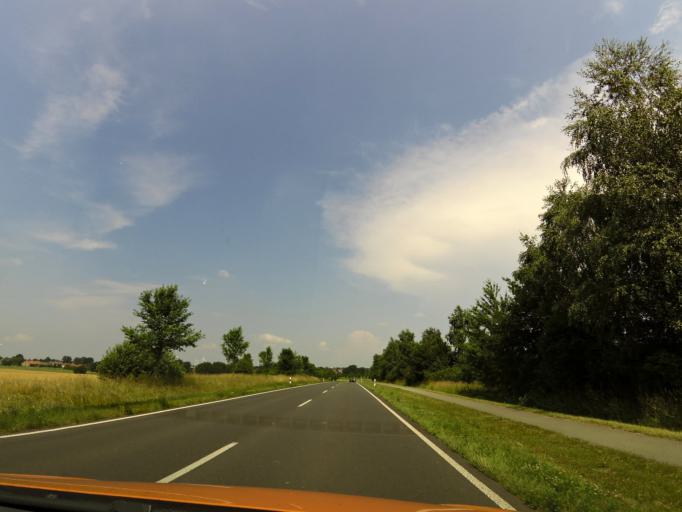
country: DE
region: Brandenburg
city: Gerdshagen
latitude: 53.1991
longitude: 12.2021
